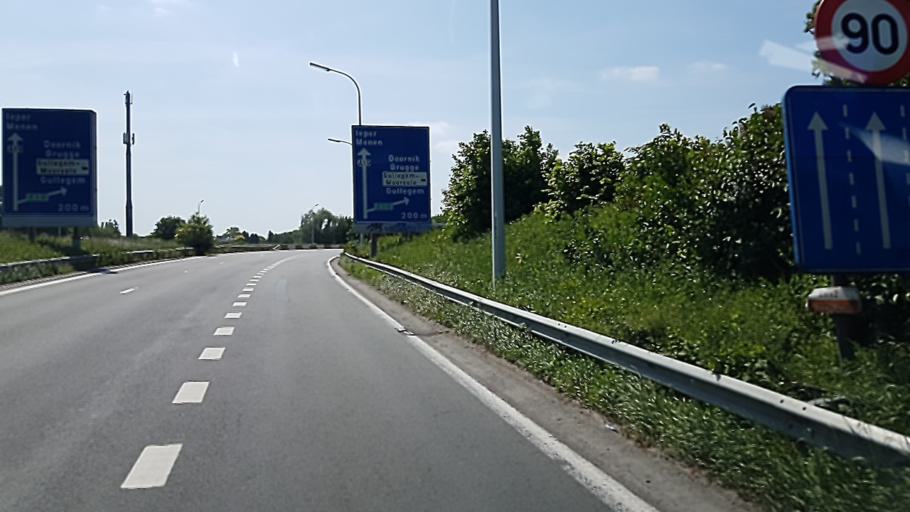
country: BE
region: Flanders
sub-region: Provincie West-Vlaanderen
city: Kortrijk
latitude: 50.8302
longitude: 3.2140
